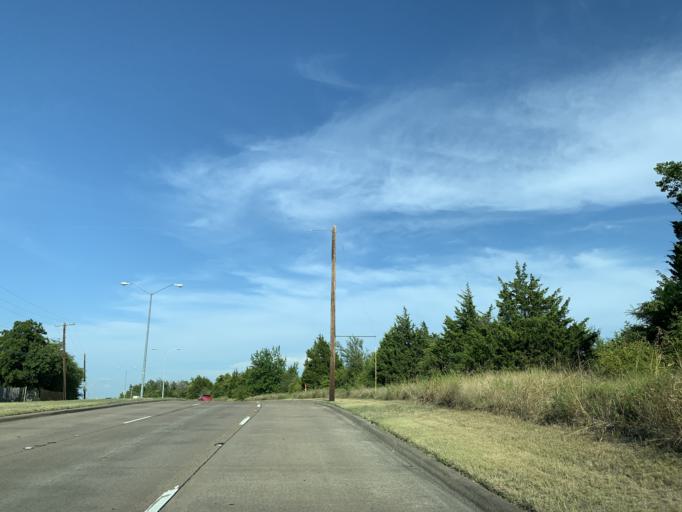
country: US
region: Texas
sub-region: Dallas County
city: Lancaster
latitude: 32.6622
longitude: -96.8039
